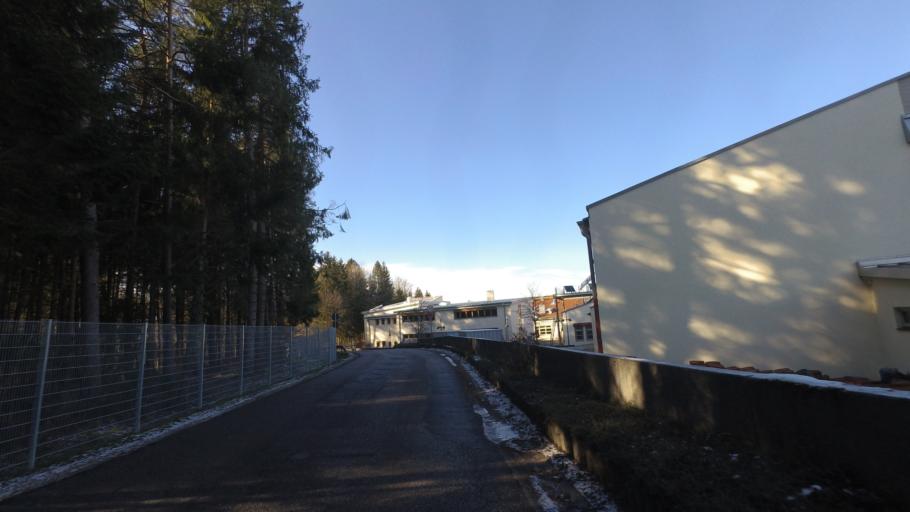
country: DE
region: Bavaria
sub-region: Upper Bavaria
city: Traunreut
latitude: 47.9581
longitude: 12.6143
